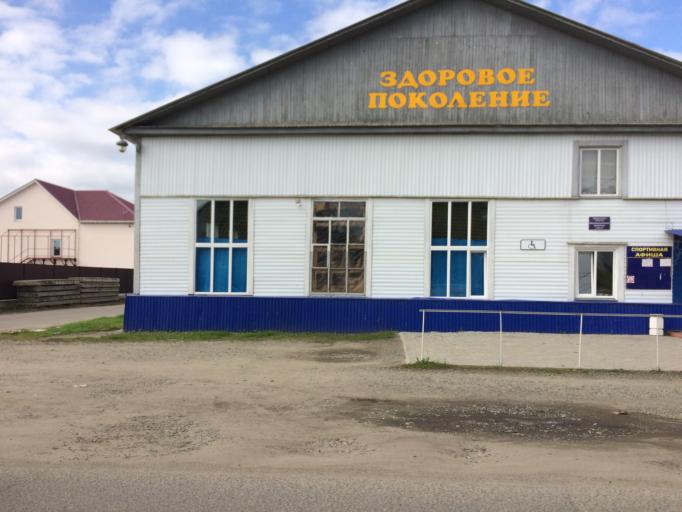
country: RU
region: Primorskiy
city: Dal'nerechensk
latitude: 45.9304
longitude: 133.7374
